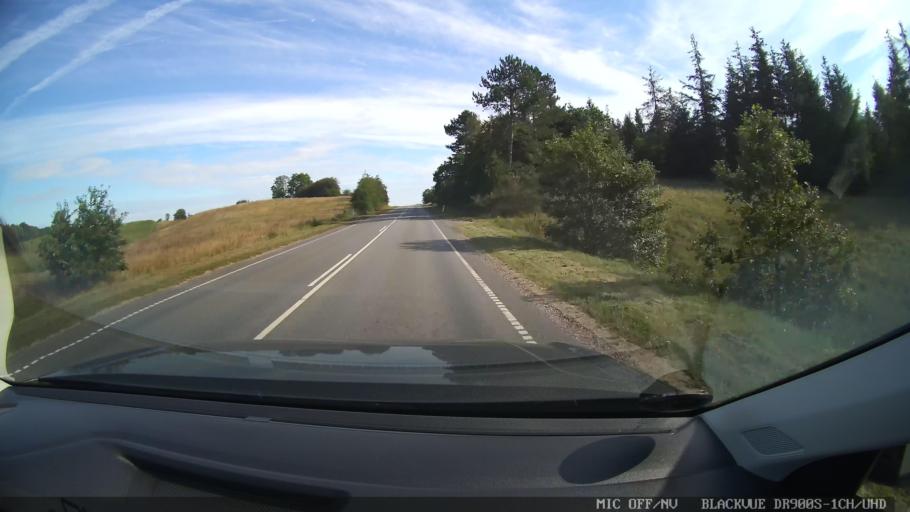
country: DK
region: North Denmark
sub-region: Mariagerfjord Kommune
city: Hadsund
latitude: 56.7961
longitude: 10.0346
